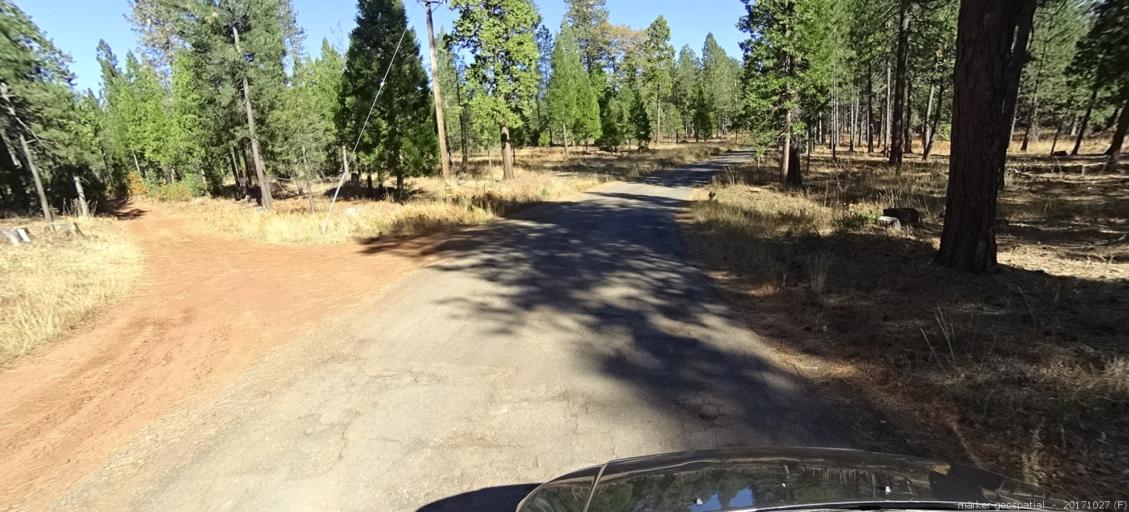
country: US
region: California
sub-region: Shasta County
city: Shingletown
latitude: 40.6142
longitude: -121.8320
